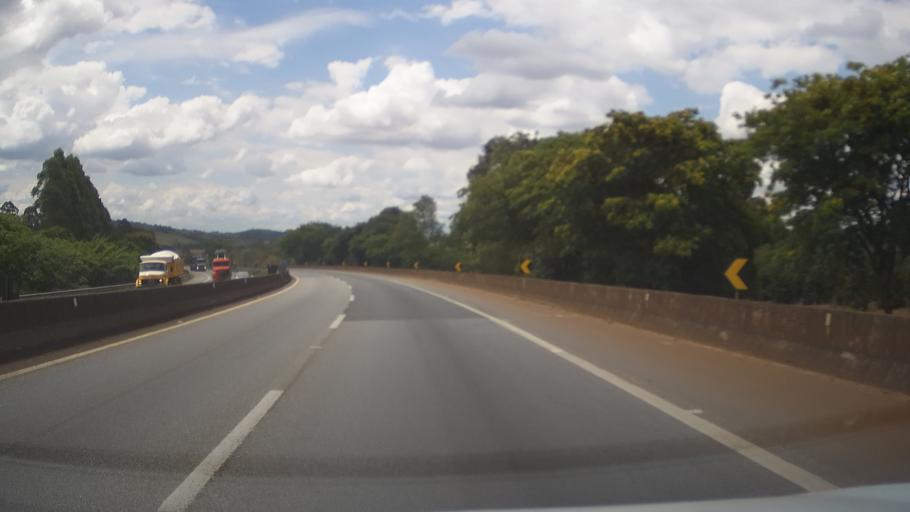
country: BR
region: Minas Gerais
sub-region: Nepomuceno
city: Nepomuceno
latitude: -21.2428
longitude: -45.1357
